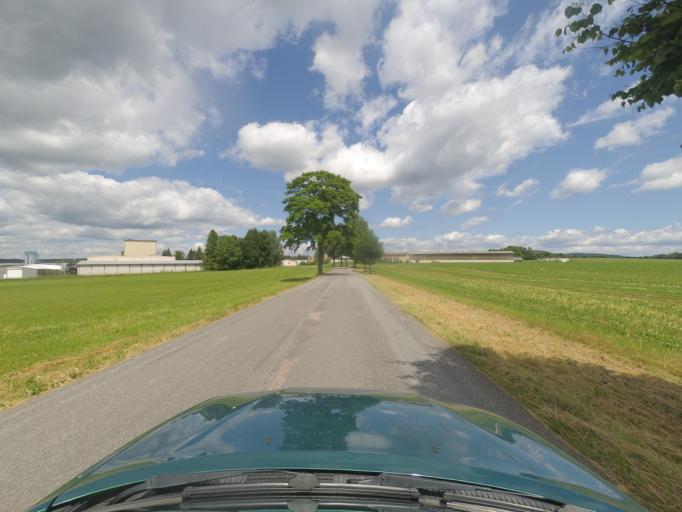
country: CZ
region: Pardubicky
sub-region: Okres Usti nad Orlici
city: Kunvald
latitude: 50.1058
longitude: 16.5343
